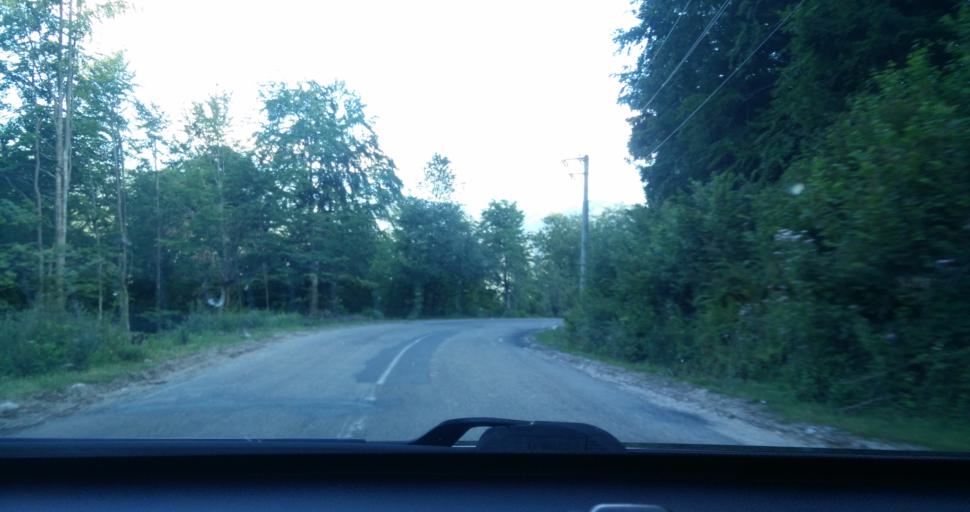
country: RO
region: Bihor
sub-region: Oras Nucet
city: Nucet
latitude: 46.4999
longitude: 22.6142
